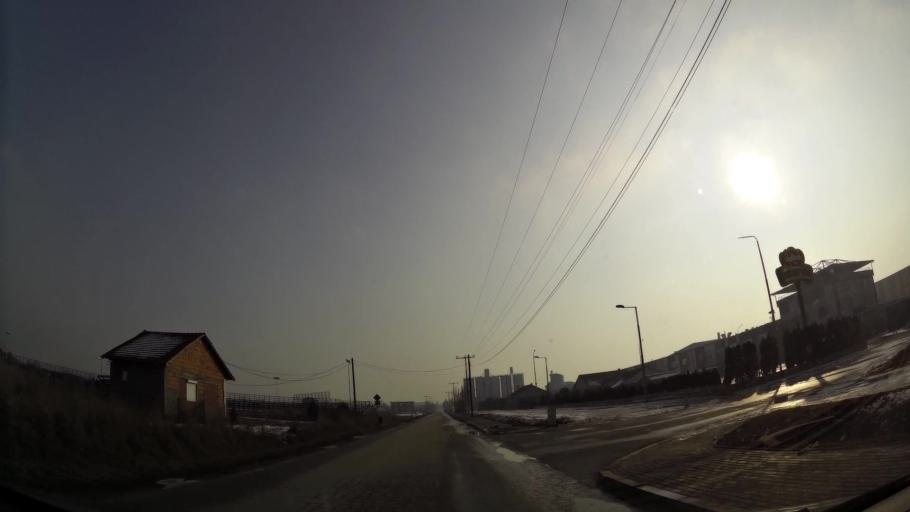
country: MK
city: Kadino
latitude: 41.9772
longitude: 21.5938
